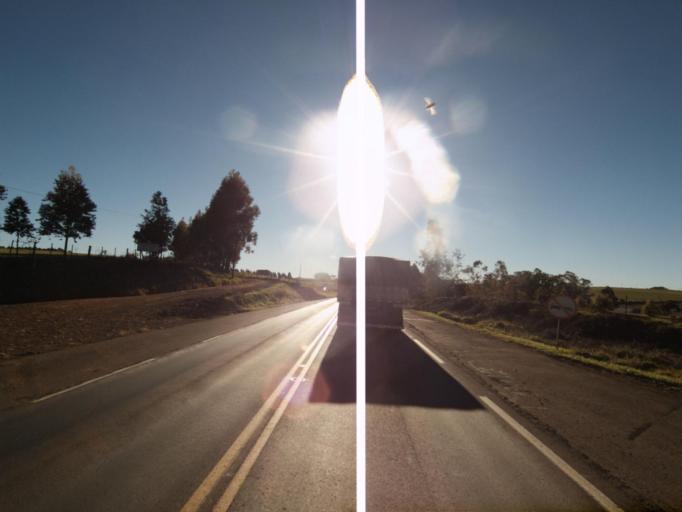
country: AR
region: Misiones
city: Bernardo de Irigoyen
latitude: -26.3057
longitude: -53.5491
